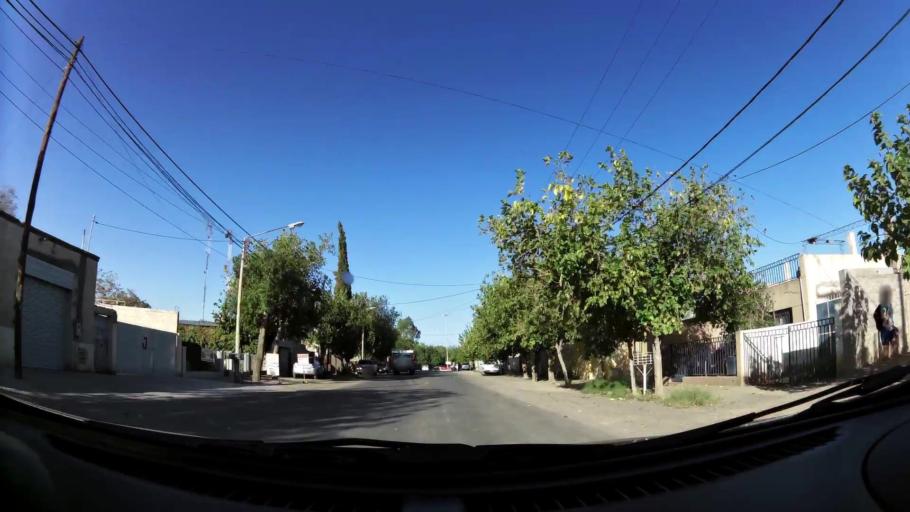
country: AR
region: San Juan
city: Villa Krause
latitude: -31.5588
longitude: -68.5162
